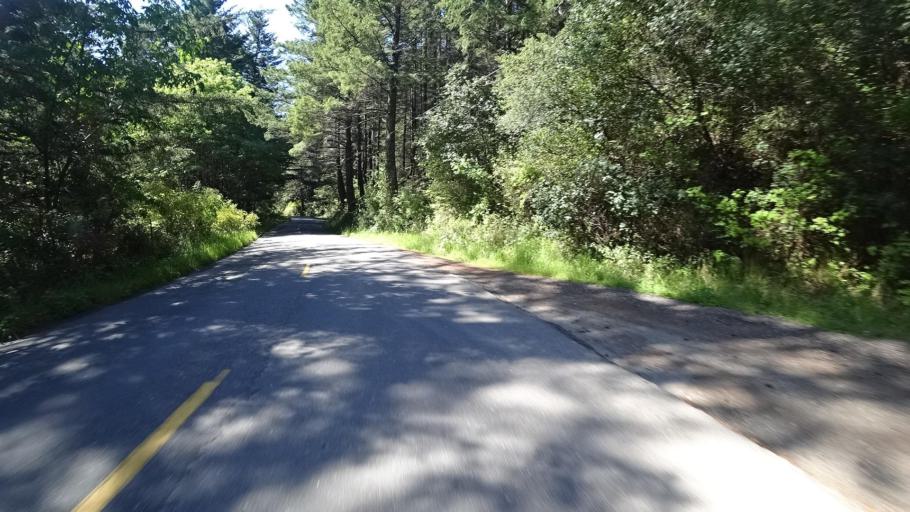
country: US
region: California
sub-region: Humboldt County
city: Rio Dell
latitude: 40.2976
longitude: -124.2509
